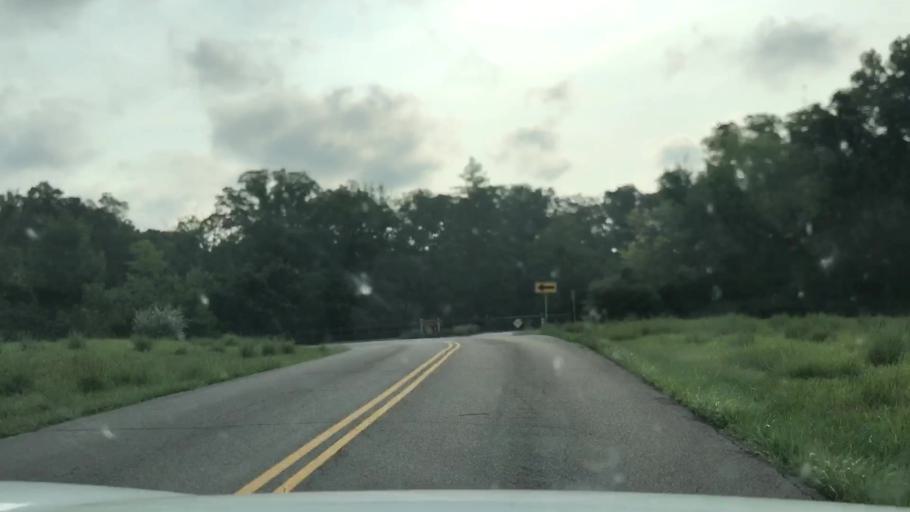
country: US
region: Missouri
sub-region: Saint Charles County
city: Cottleville
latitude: 38.7044
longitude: -90.6433
